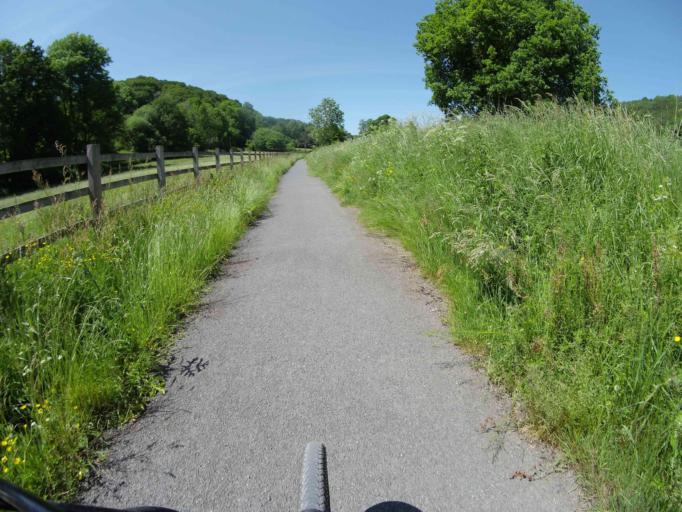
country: GB
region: England
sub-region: Devon
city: Bovey Tracey
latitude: 50.6496
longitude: -3.7434
